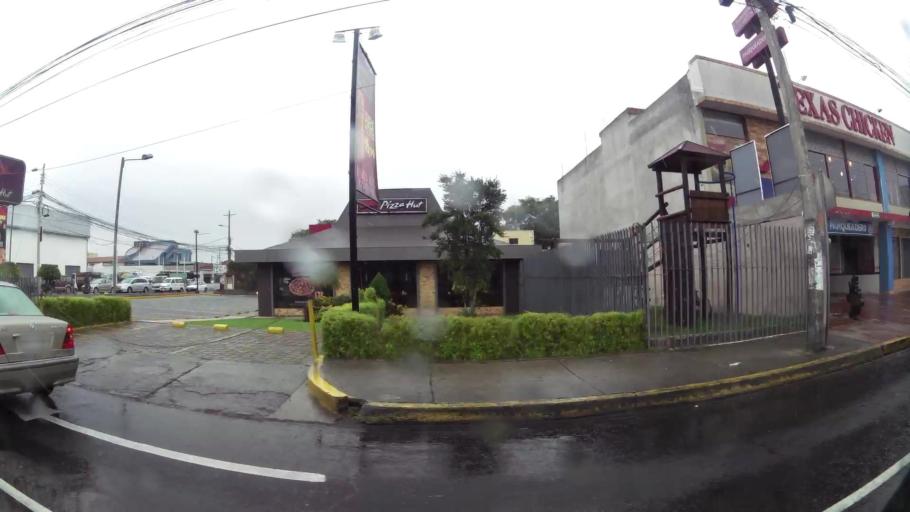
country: EC
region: Pichincha
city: Sangolqui
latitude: -0.3013
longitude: -78.4576
